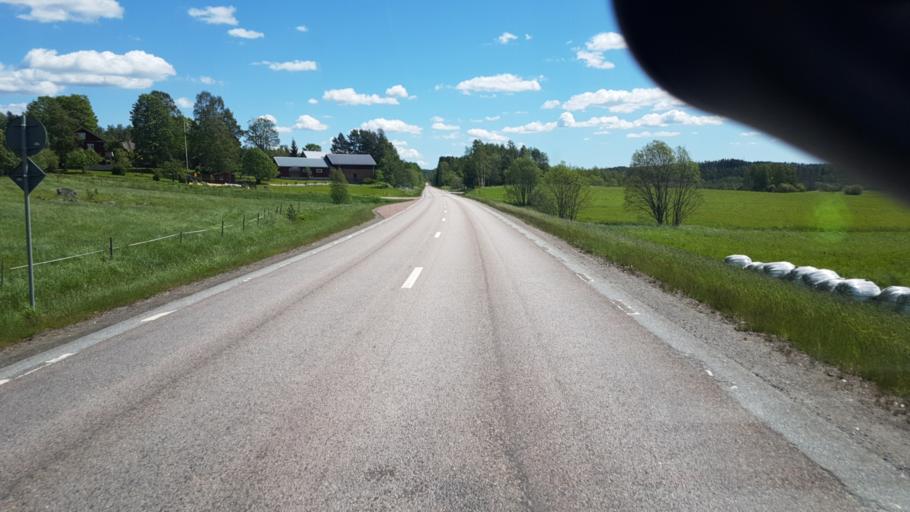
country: SE
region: Vaermland
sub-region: Arvika Kommun
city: Arvika
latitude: 59.6366
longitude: 12.7939
